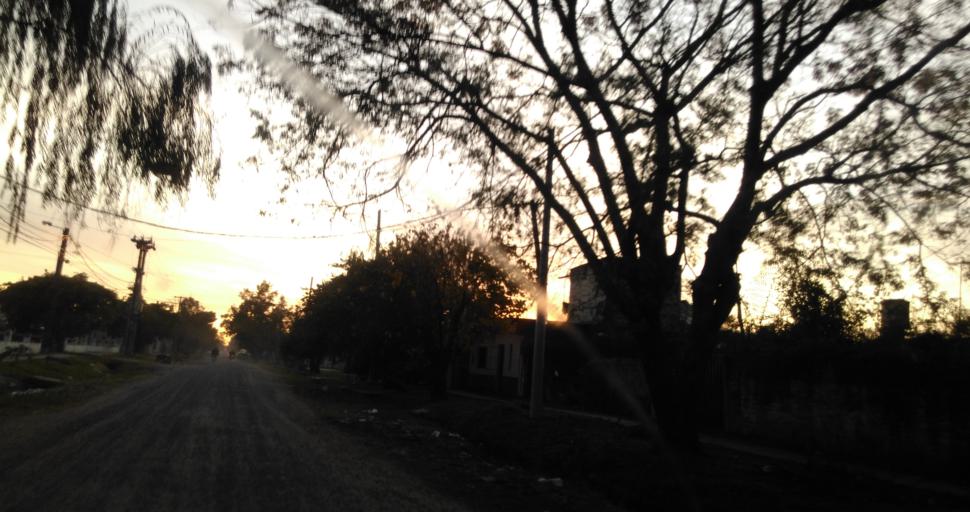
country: AR
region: Chaco
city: Resistencia
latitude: -27.4708
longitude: -58.9980
